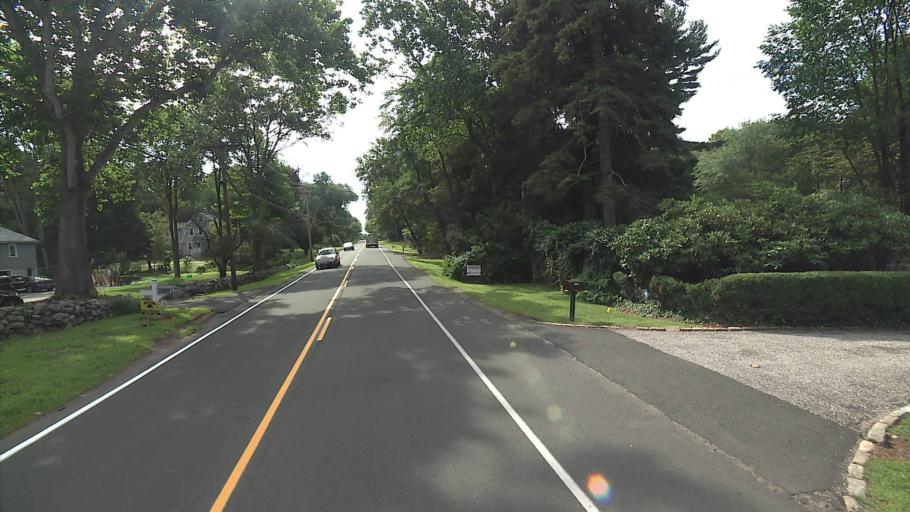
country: US
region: Connecticut
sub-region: New Haven County
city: Woodbridge
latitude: 41.3429
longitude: -73.0146
